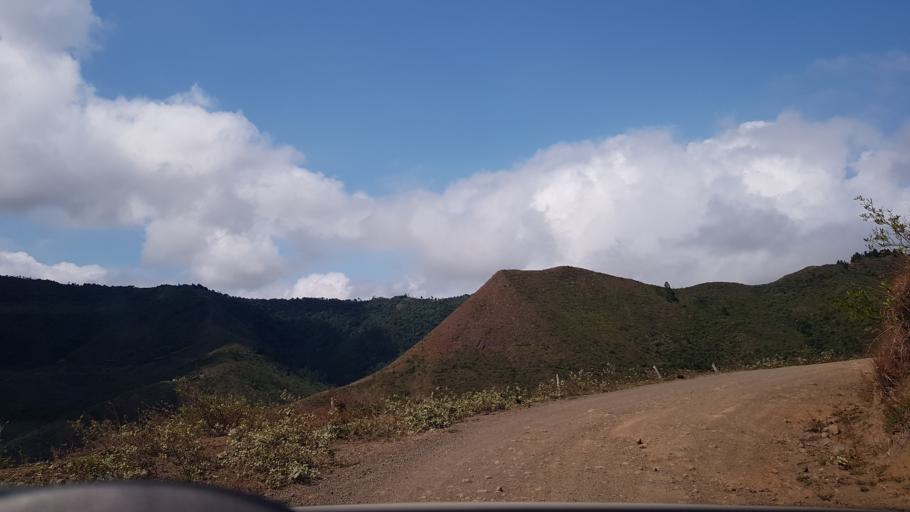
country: CO
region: Valle del Cauca
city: Yumbo
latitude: 3.6509
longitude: -76.5110
